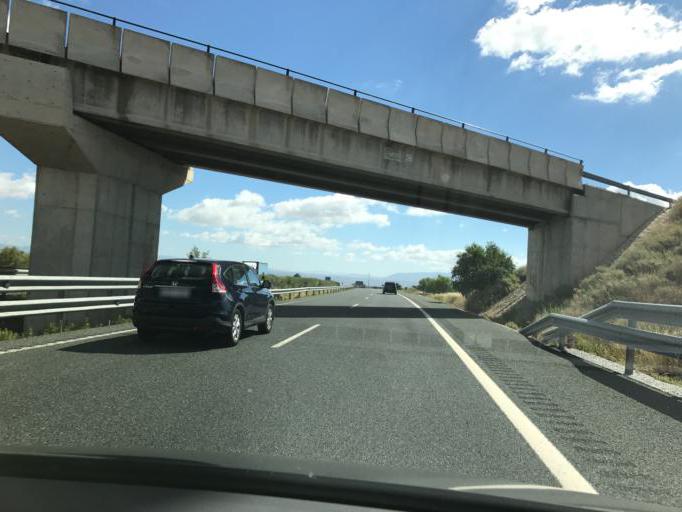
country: ES
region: Andalusia
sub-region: Provincia de Granada
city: Baza
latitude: 37.4971
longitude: -2.8168
